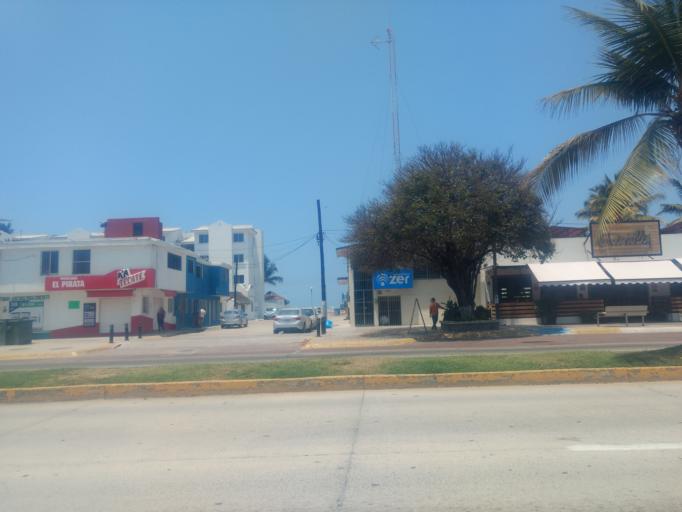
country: MX
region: Colima
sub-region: Manzanillo
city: Manzanillo
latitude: 19.0983
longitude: -104.3226
